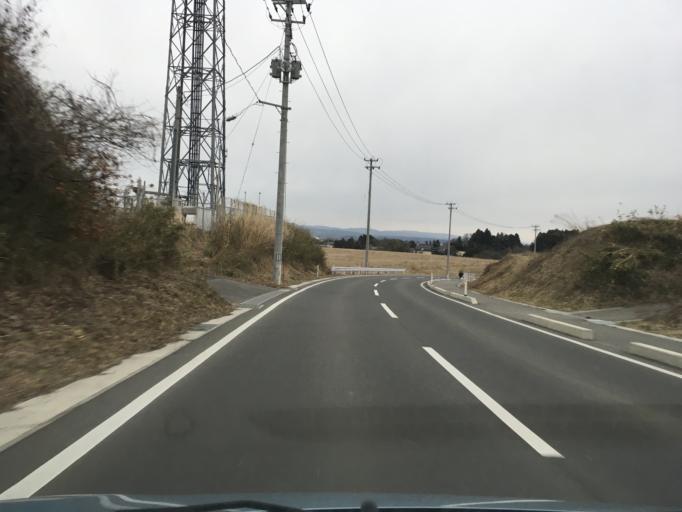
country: JP
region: Miyagi
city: Wakuya
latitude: 38.6959
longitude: 141.1706
